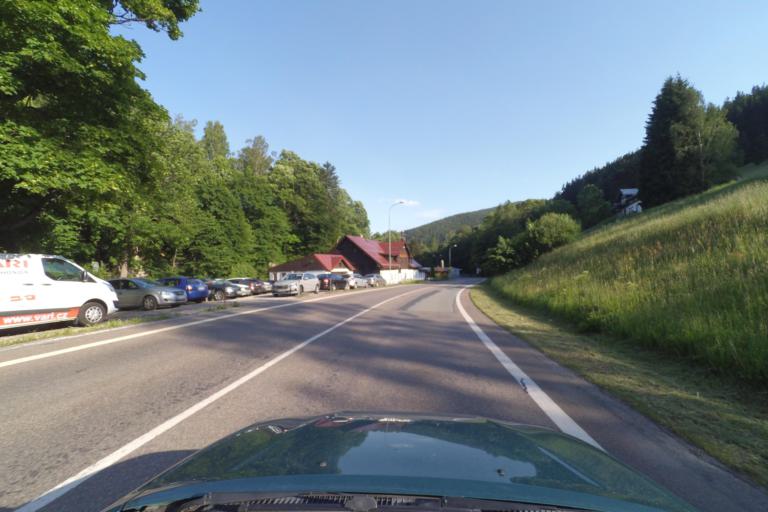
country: CZ
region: Kralovehradecky
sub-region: Okres Trutnov
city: Svoboda nad Upou
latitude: 50.6877
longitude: 15.7799
